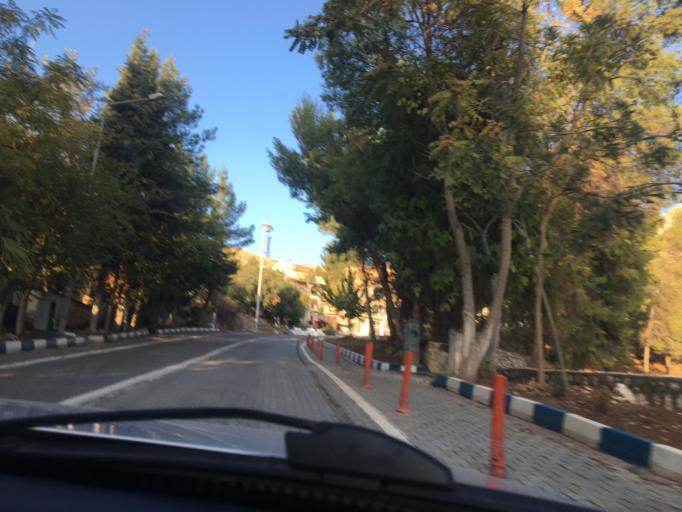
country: TR
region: Sanliurfa
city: Halfeti
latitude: 37.2435
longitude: 37.8707
